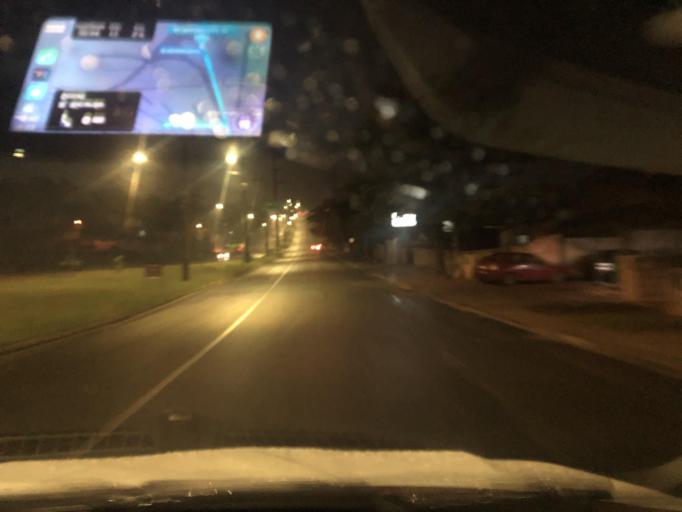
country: BR
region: Santa Catarina
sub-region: Joinville
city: Joinville
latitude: -26.3691
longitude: -48.8327
